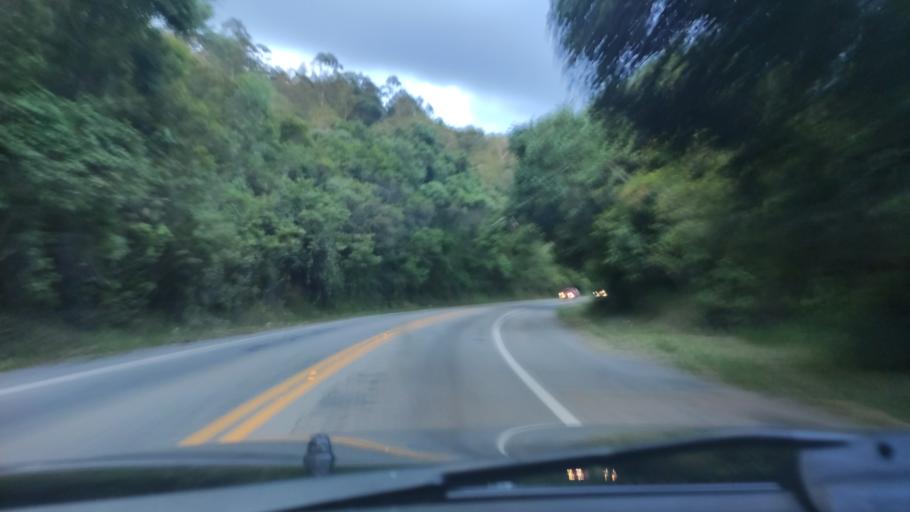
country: BR
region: Sao Paulo
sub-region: Braganca Paulista
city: Braganca Paulista
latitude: -22.8230
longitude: -46.5541
